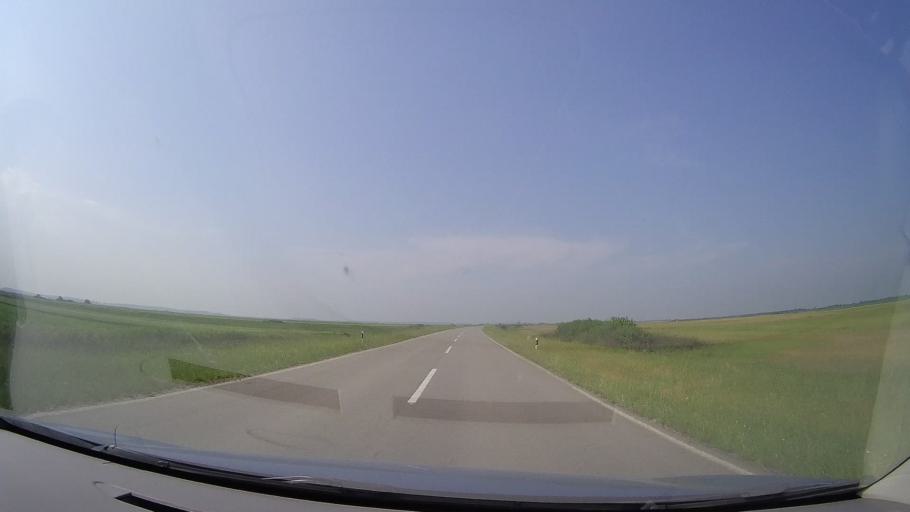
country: RS
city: Jasa Tomic
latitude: 45.4173
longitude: 20.8332
